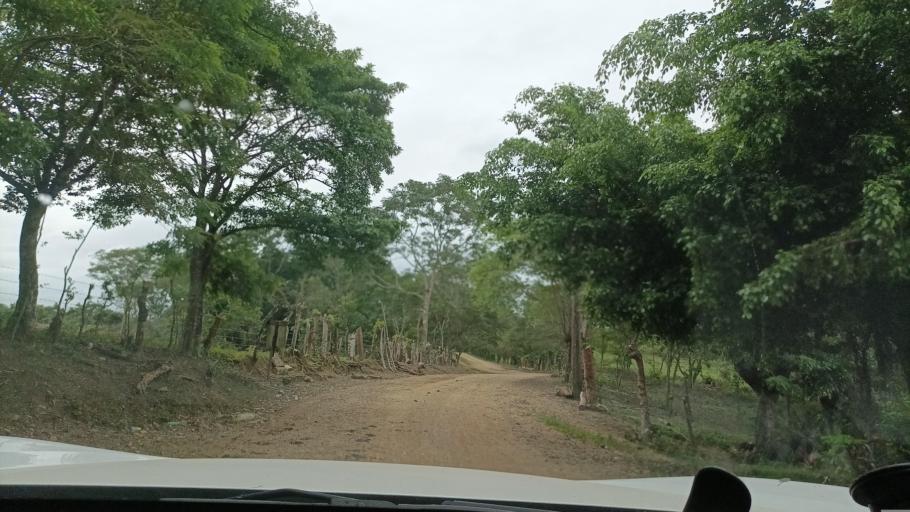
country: MX
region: Veracruz
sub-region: Uxpanapa
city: Poblado 10
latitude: 17.5535
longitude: -94.4256
